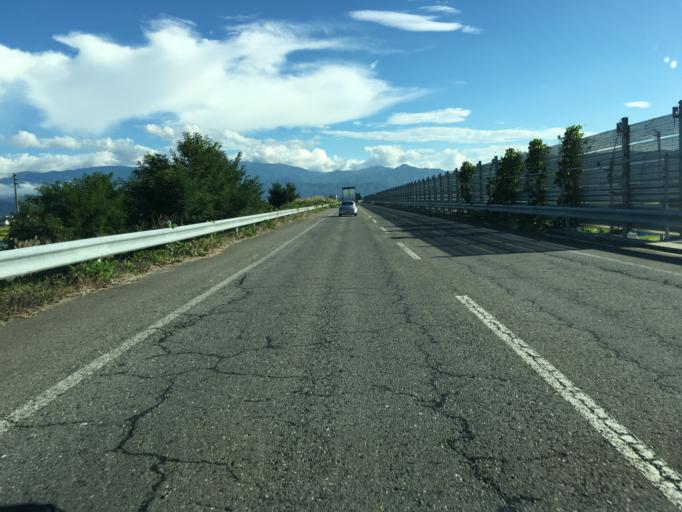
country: JP
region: Yamagata
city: Yonezawa
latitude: 37.9414
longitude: 140.1115
